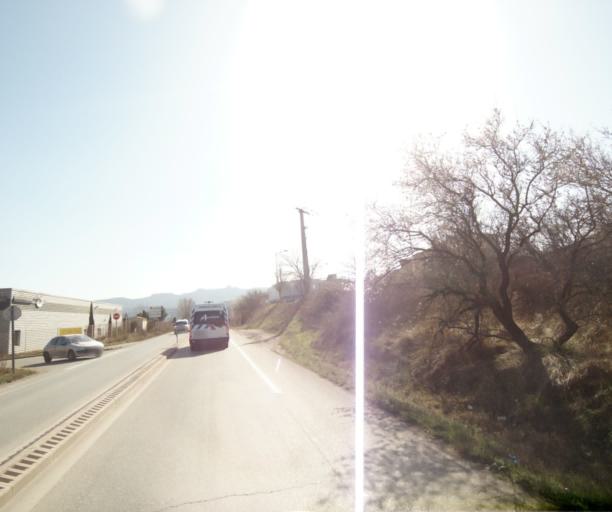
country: FR
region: Provence-Alpes-Cote d'Azur
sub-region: Departement des Bouches-du-Rhone
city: Gardanne
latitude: 43.4505
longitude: 5.4558
